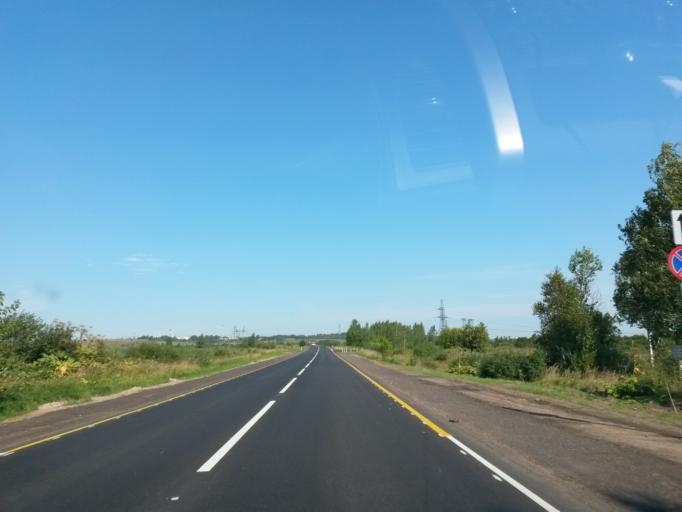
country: RU
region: Jaroslavl
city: Yaroslavl
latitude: 57.5230
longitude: 39.8841
